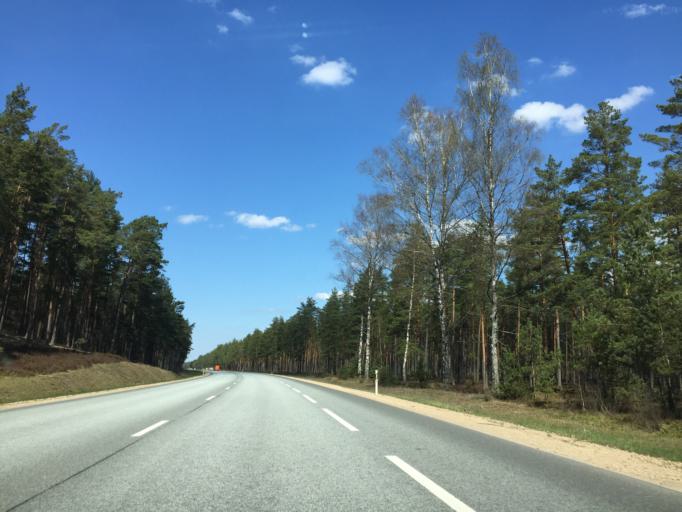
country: LV
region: Carnikava
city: Carnikava
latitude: 57.1581
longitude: 24.3463
